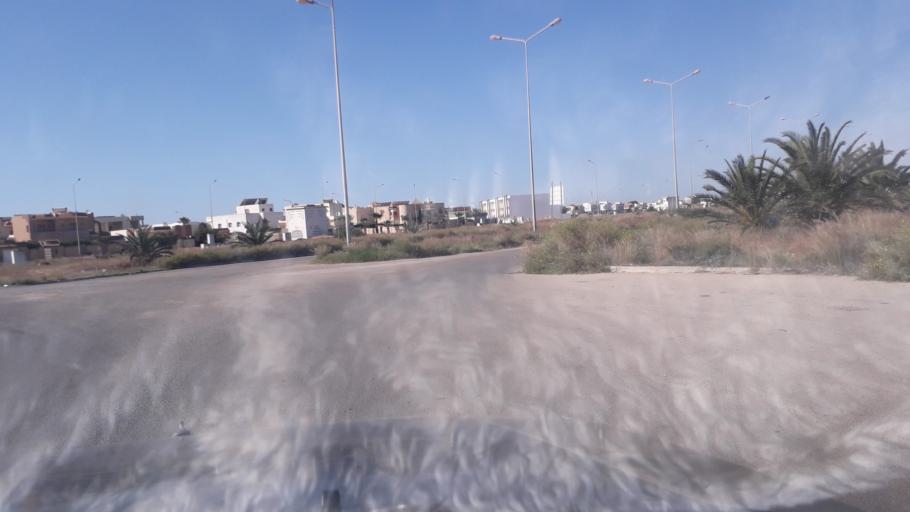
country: TN
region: Safaqis
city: Al Qarmadah
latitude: 34.8317
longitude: 10.7554
